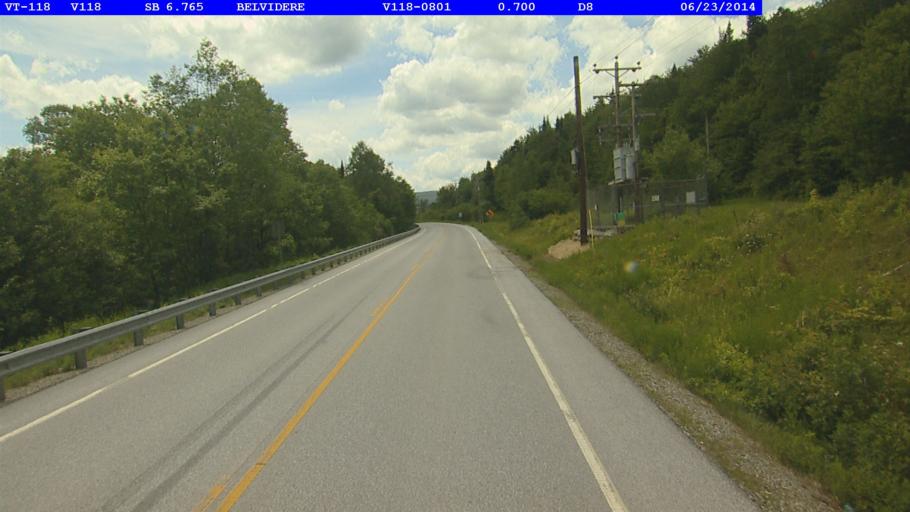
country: US
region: Vermont
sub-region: Lamoille County
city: Johnson
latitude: 44.7698
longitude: -72.6230
